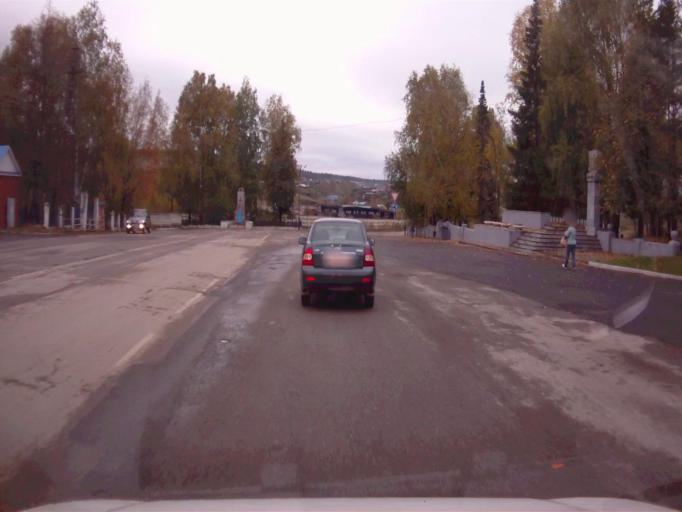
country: RU
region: Chelyabinsk
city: Nyazepetrovsk
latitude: 56.0540
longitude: 59.5950
